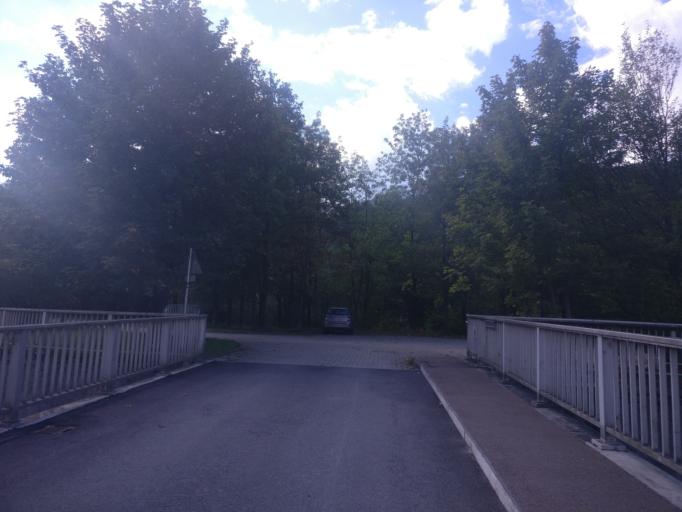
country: AT
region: Salzburg
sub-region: Politischer Bezirk Sankt Johann im Pongau
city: Bischofshofen
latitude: 47.4068
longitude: 13.2202
